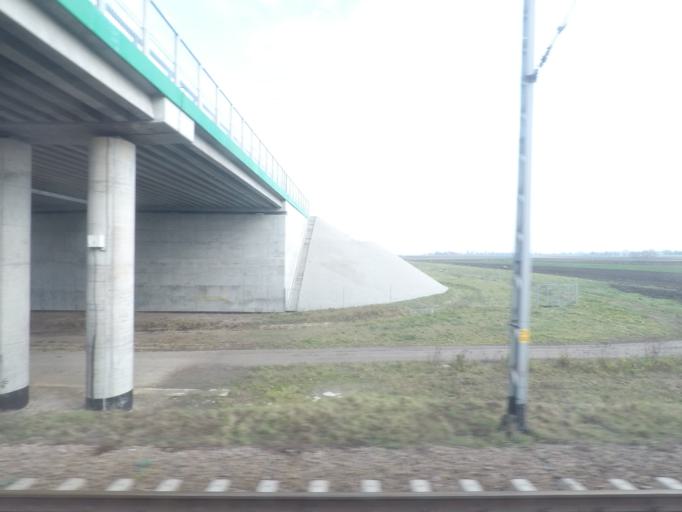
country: PL
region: Subcarpathian Voivodeship
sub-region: Powiat jaroslawski
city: Sosnica
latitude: 49.9132
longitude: 22.8462
